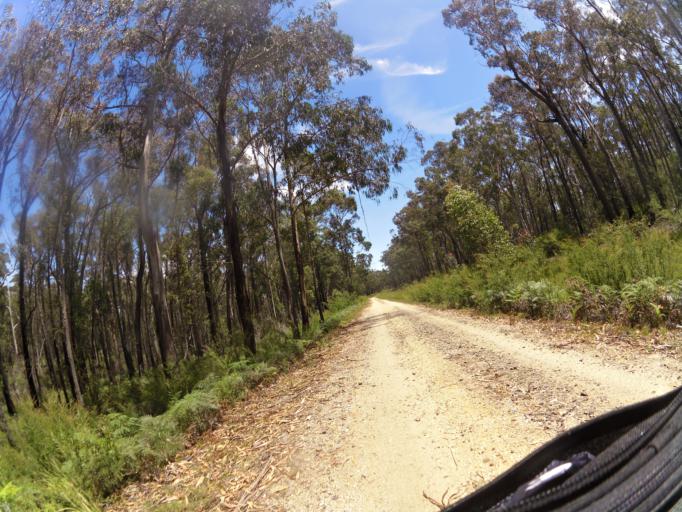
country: AU
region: Victoria
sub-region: East Gippsland
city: Lakes Entrance
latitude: -37.7588
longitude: 147.9415
